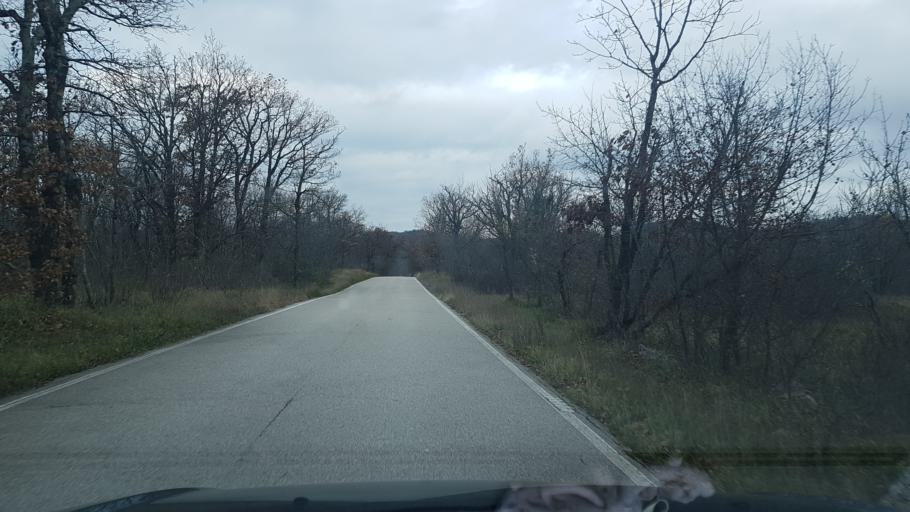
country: IT
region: Friuli Venezia Giulia
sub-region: Provincia di Trieste
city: Zolla
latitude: 45.7068
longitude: 13.8200
